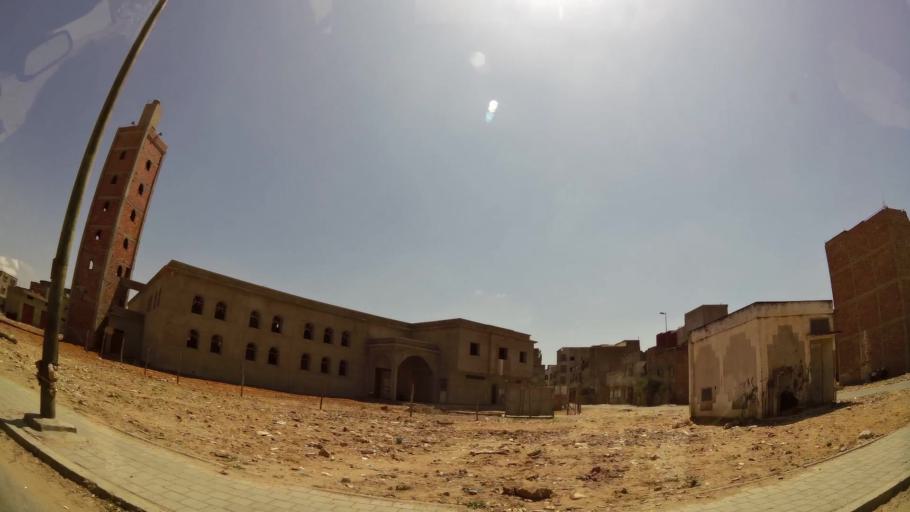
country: MA
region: Gharb-Chrarda-Beni Hssen
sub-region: Kenitra Province
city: Kenitra
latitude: 34.2288
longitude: -6.5440
